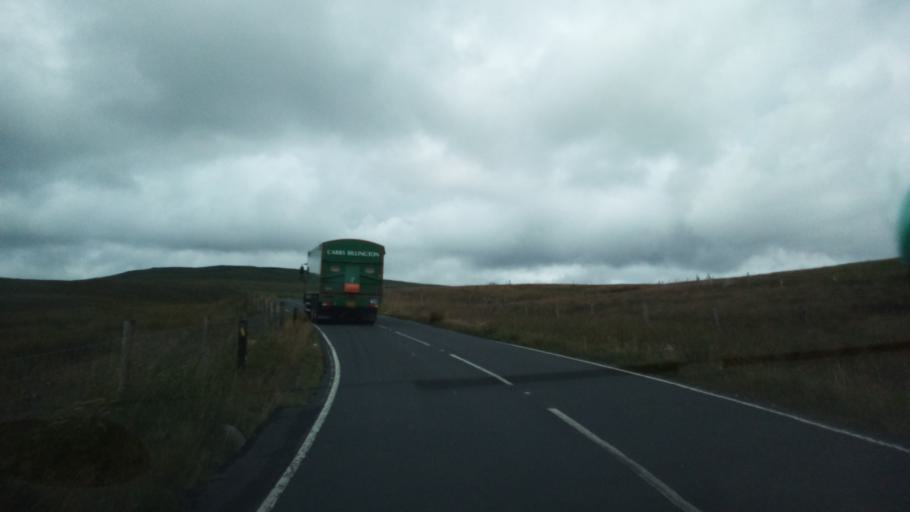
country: GB
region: England
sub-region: North Yorkshire
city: Ingleton
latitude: 54.2430
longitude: -2.3159
